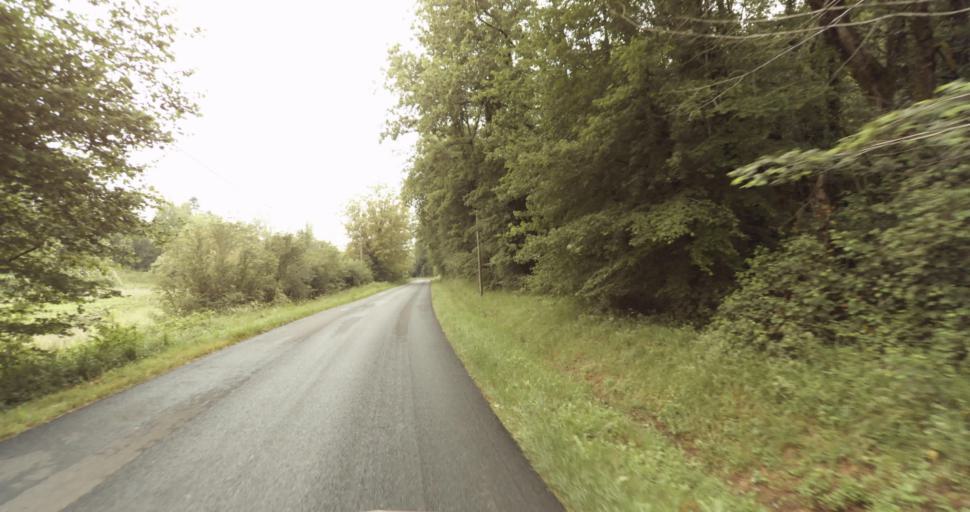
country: FR
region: Aquitaine
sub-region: Departement de la Dordogne
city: Lalinde
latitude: 44.8578
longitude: 0.7747
